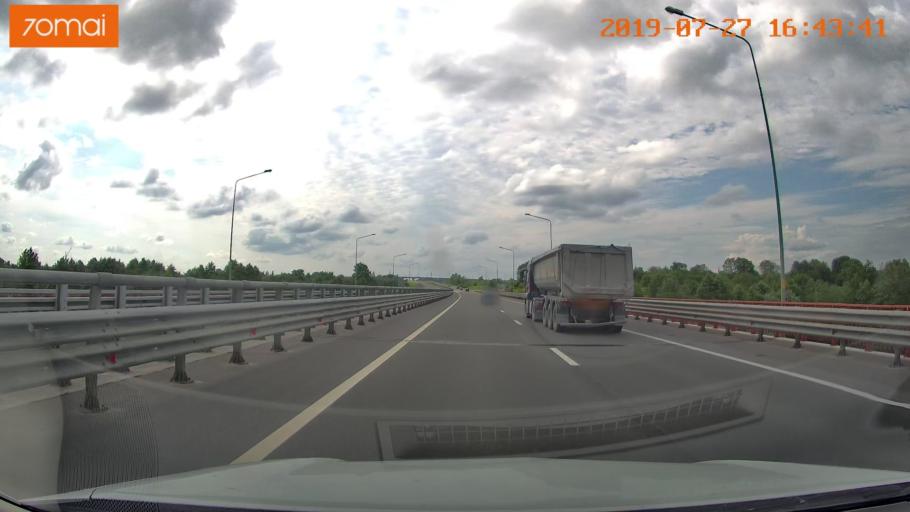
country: RU
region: Kaliningrad
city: Gvardeysk
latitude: 54.6720
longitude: 21.0967
